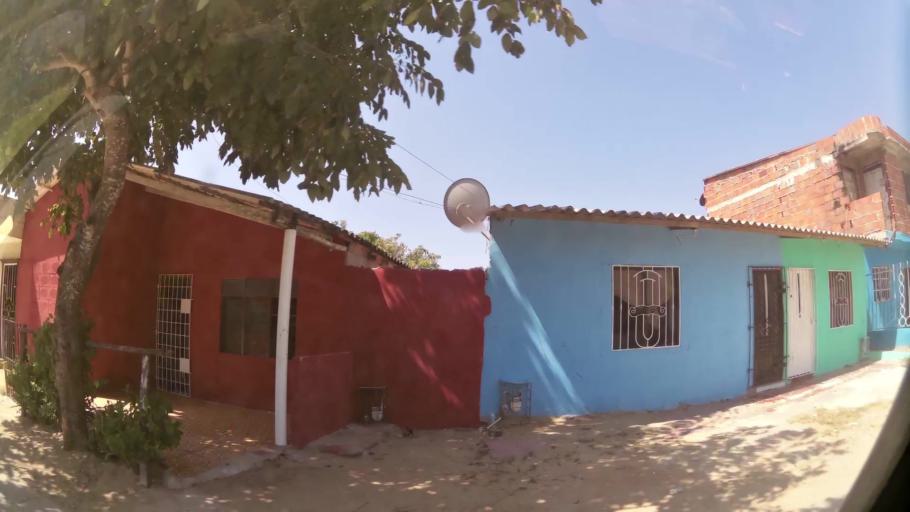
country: CO
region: Atlantico
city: Barranquilla
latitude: 10.9671
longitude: -74.8230
